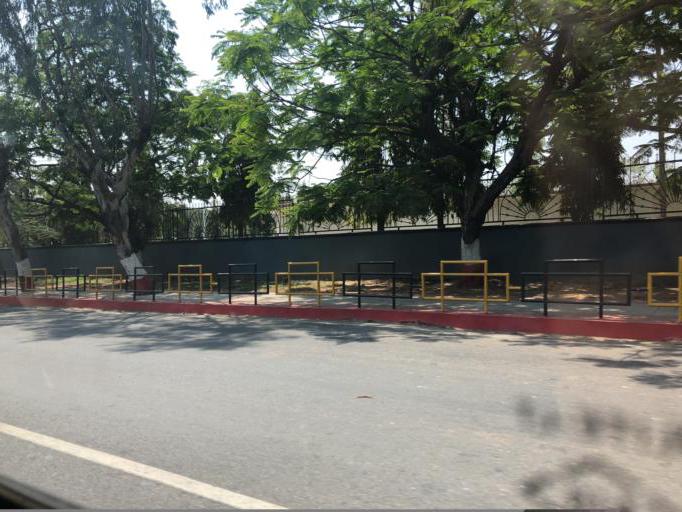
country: IN
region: Andhra Pradesh
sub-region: Vishakhapatnam
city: Yarada
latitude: 17.6930
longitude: 83.2683
